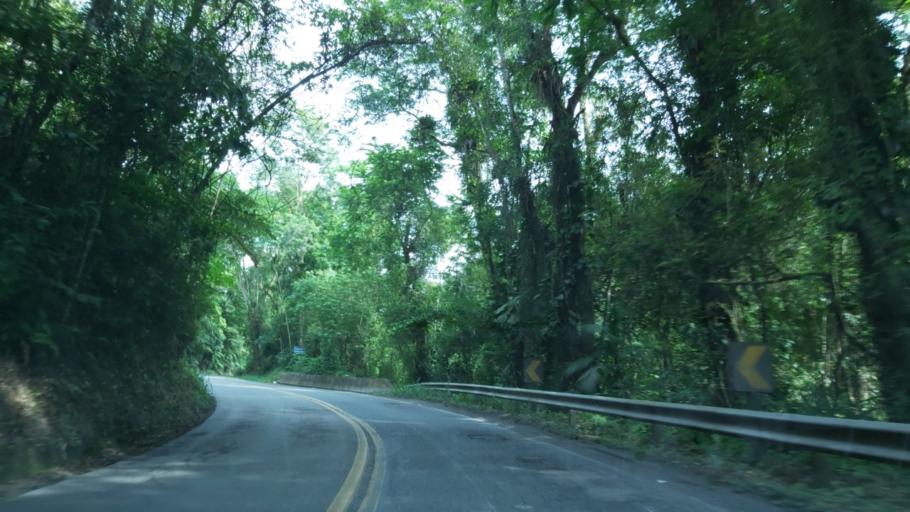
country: BR
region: Sao Paulo
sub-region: Juquia
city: Juquia
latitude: -24.0902
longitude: -47.6154
